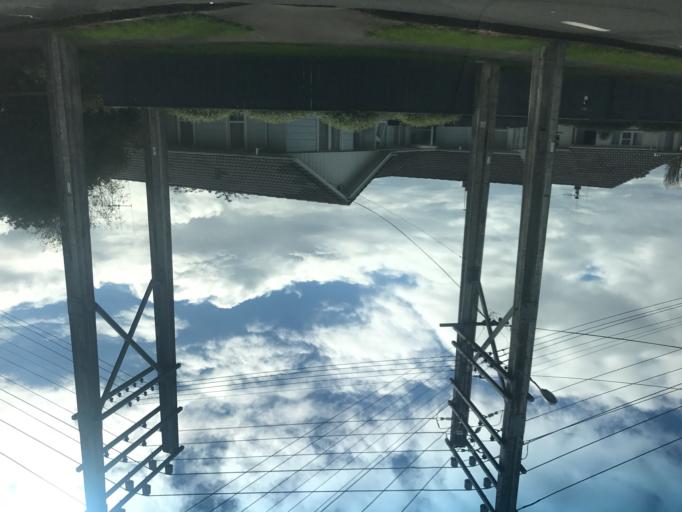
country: NZ
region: Wellington
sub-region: Kapiti Coast District
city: Otaki
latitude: -40.7635
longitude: 175.1523
